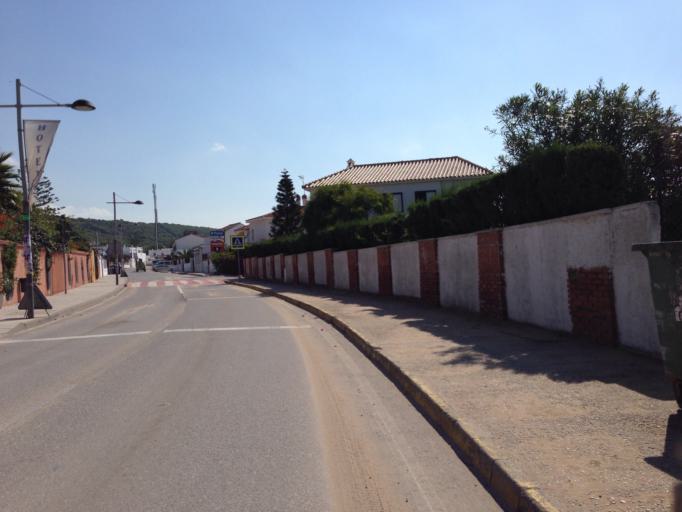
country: ES
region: Andalusia
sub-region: Provincia de Cadiz
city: Vejer de la Frontera
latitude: 36.1859
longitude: -6.0141
